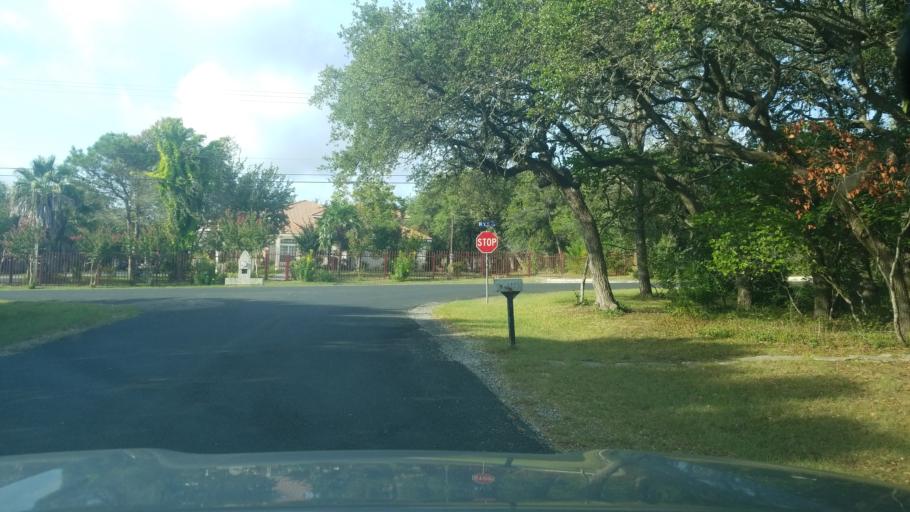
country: US
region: Texas
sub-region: Bexar County
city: Timberwood Park
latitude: 29.6974
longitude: -98.5180
